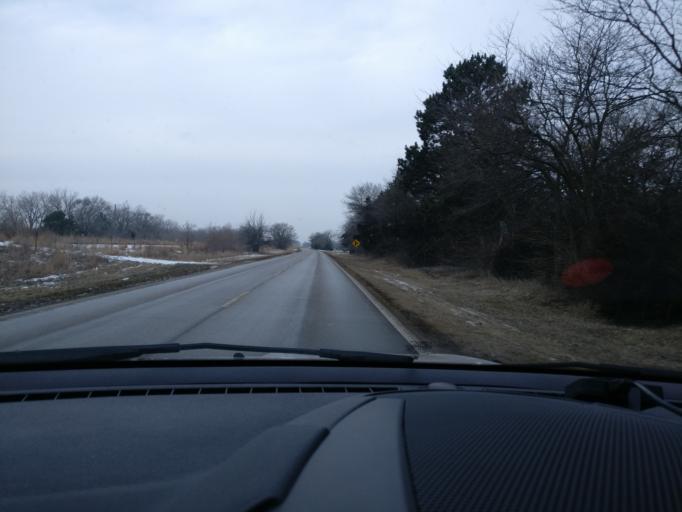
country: US
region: Nebraska
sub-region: Dodge County
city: Fremont
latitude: 41.4484
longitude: -96.5661
